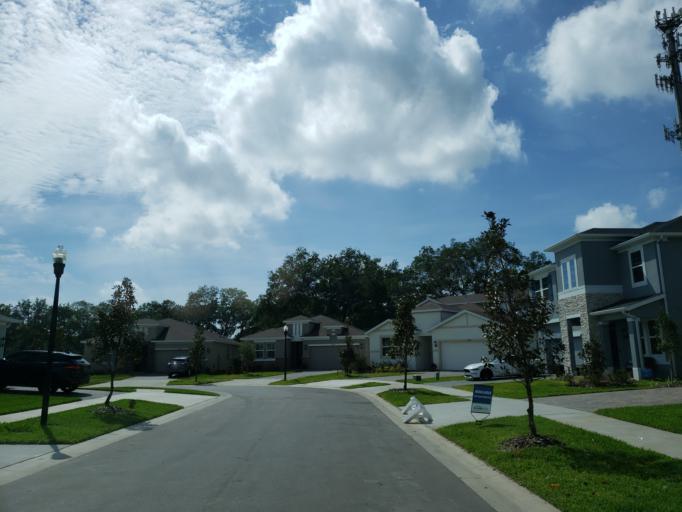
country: US
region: Florida
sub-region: Hillsborough County
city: Riverview
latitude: 27.8986
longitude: -82.3210
